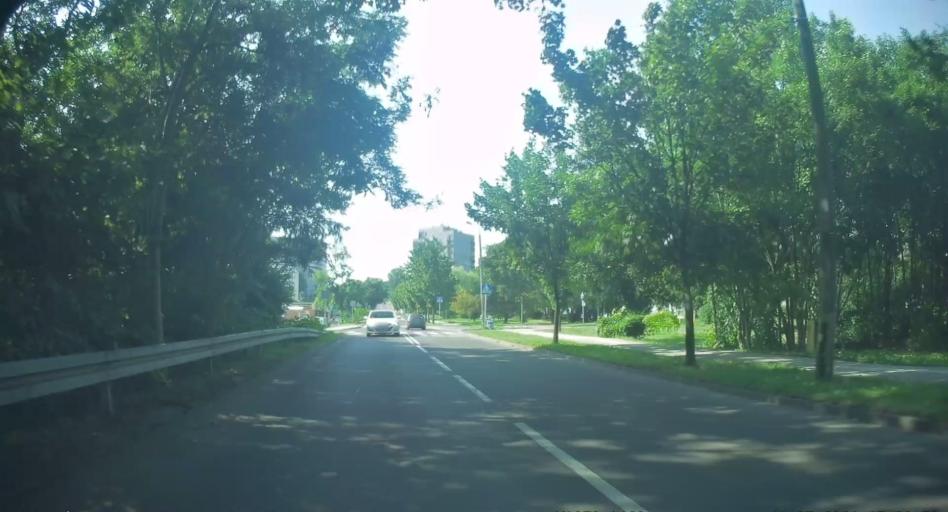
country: PL
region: Silesian Voivodeship
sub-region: Swietochlowice
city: Swietochlowice
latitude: 50.3093
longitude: 18.9199
